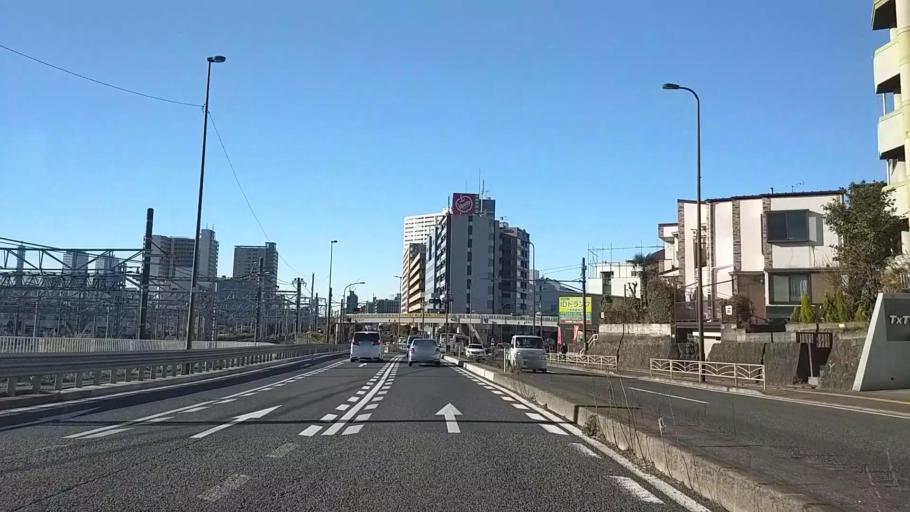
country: JP
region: Kanagawa
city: Yokohama
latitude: 35.4824
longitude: 139.6369
